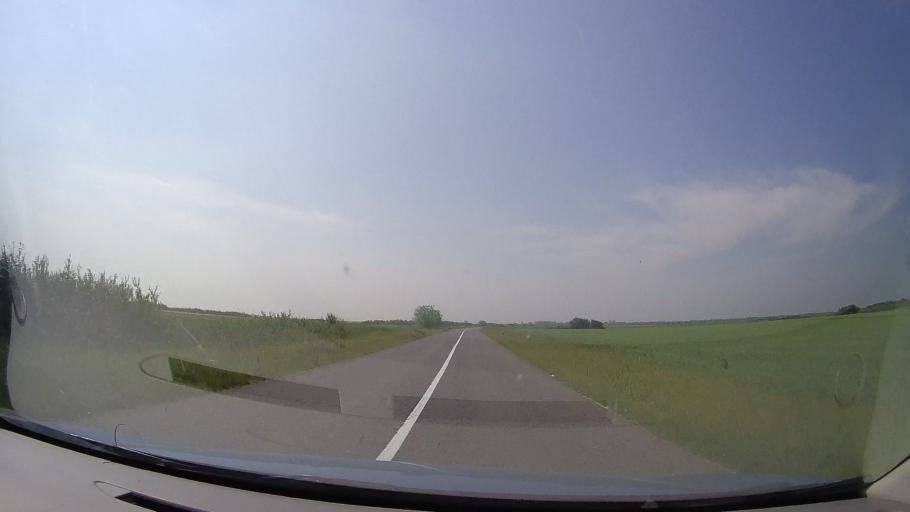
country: RS
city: Jarkovac
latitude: 45.2945
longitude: 20.7642
